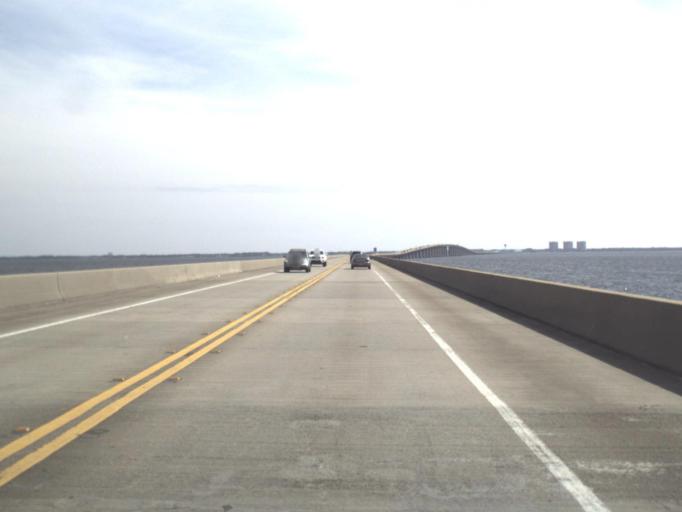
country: US
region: Florida
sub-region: Okaloosa County
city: Niceville
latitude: 30.4505
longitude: -86.4159
